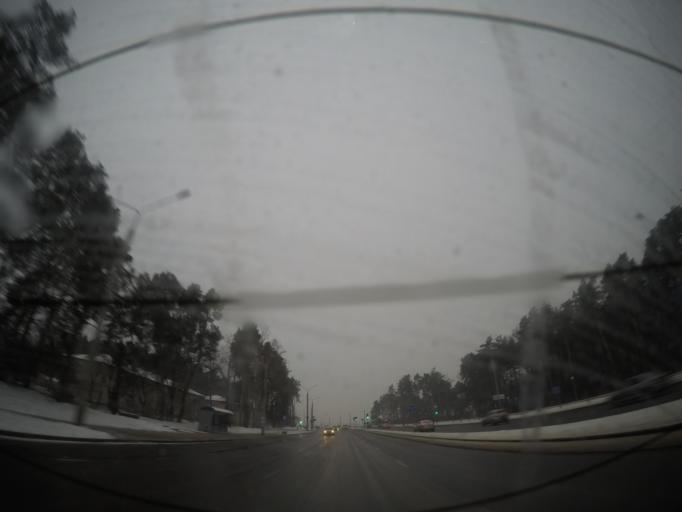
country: BY
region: Grodnenskaya
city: Hrodna
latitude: 53.6337
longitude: 23.8081
